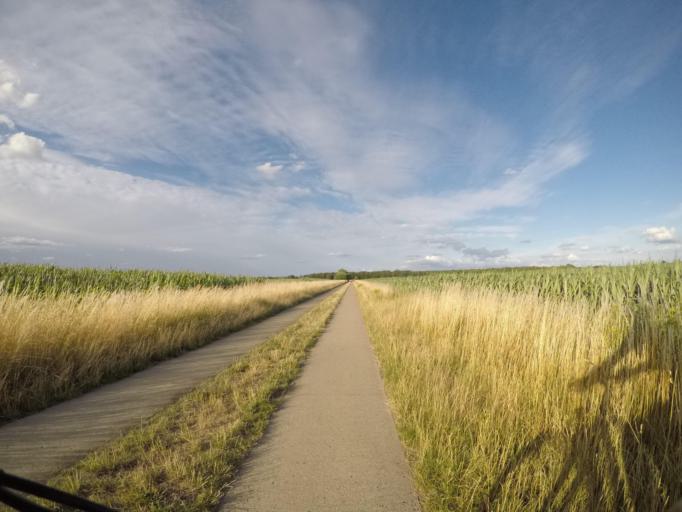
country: DE
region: Lower Saxony
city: Hitzacker
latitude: 53.2196
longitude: 11.0737
